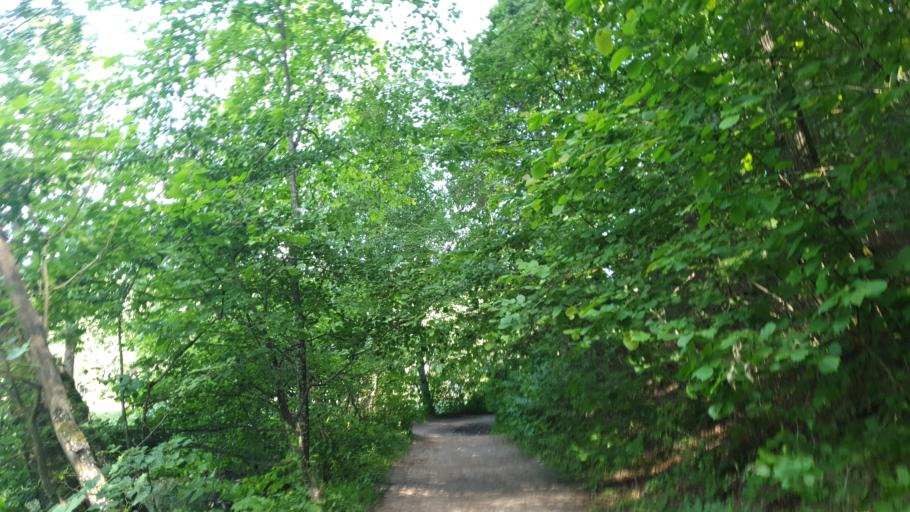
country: LT
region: Vilnius County
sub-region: Vilnius
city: Fabijoniskes
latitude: 54.7845
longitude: 25.3312
